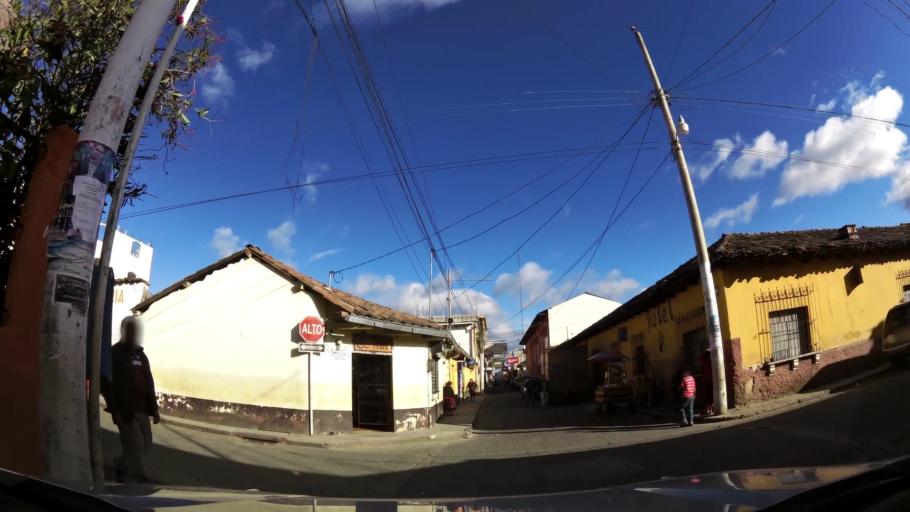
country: GT
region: Quiche
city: Chichicastenango
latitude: 14.9436
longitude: -91.1118
